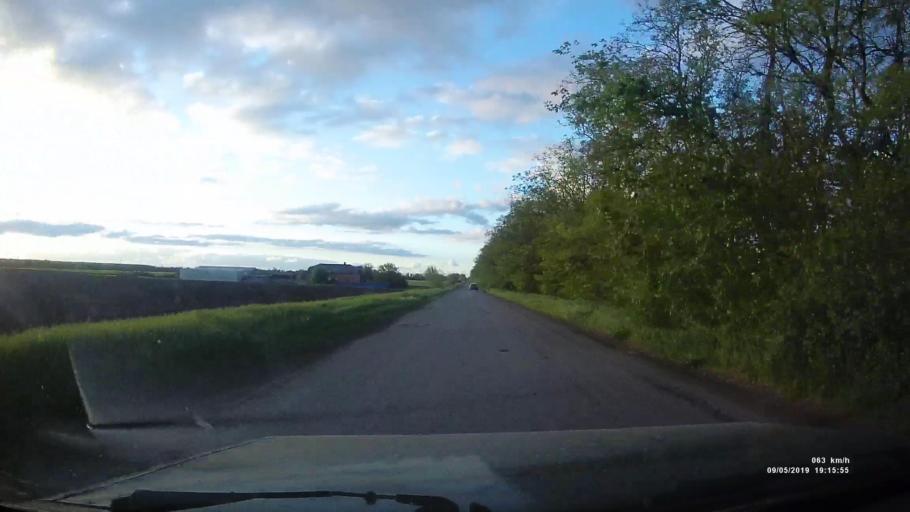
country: RU
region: Krasnodarskiy
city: Kanelovskaya
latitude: 46.7731
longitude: 39.2114
